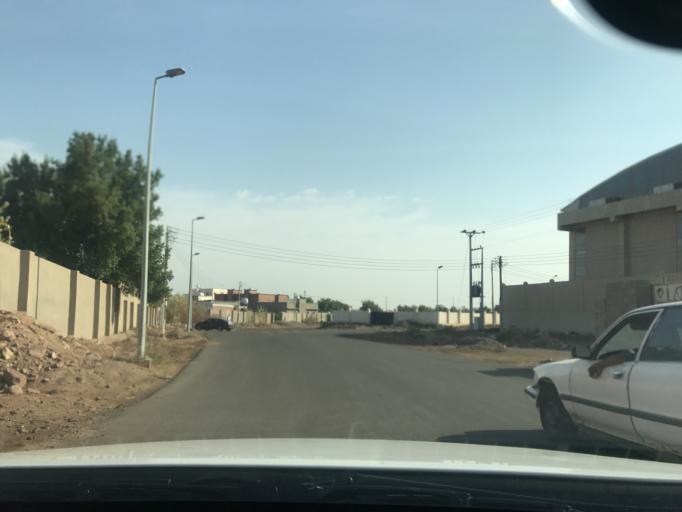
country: SA
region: Makkah
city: Al Jumum
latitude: 21.4497
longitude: 39.5381
